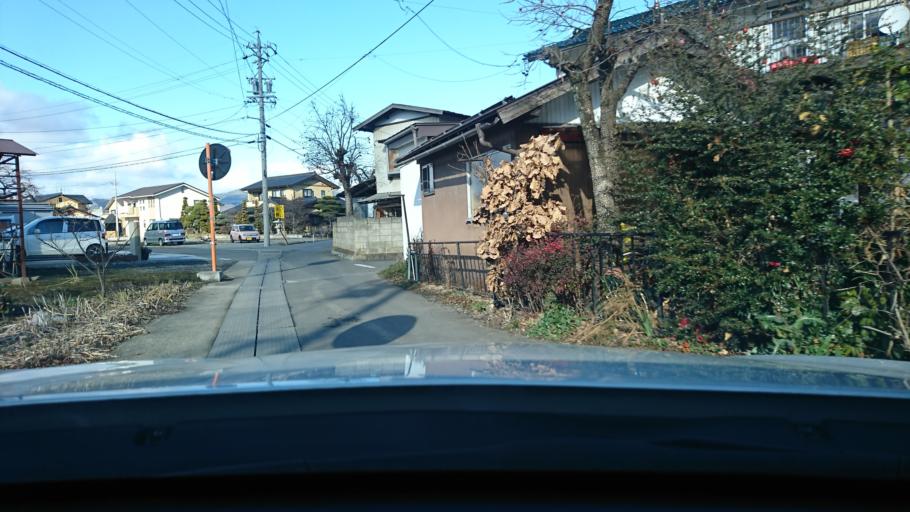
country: JP
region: Nagano
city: Nagano-shi
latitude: 36.5471
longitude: 138.1453
